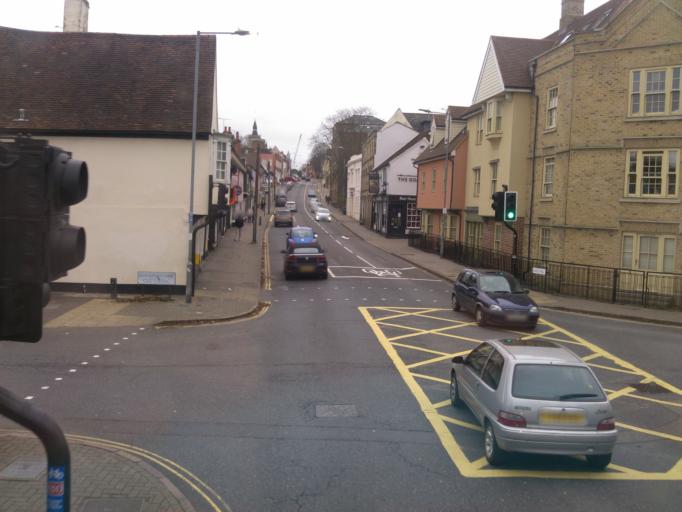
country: GB
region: England
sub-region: Essex
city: Colchester
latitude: 51.8899
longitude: 0.9122
